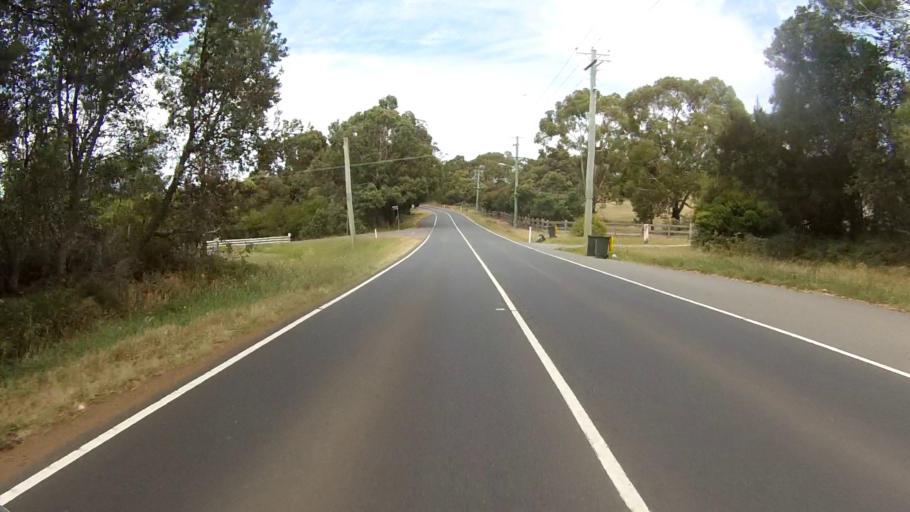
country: AU
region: Tasmania
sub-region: Clarence
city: Acton Park
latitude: -42.8779
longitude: 147.4822
